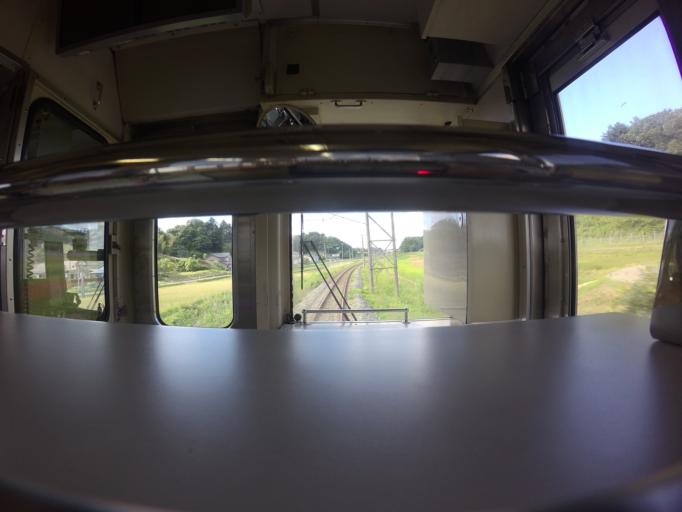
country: JP
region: Fukushima
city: Namie
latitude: 37.6121
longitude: 140.9857
